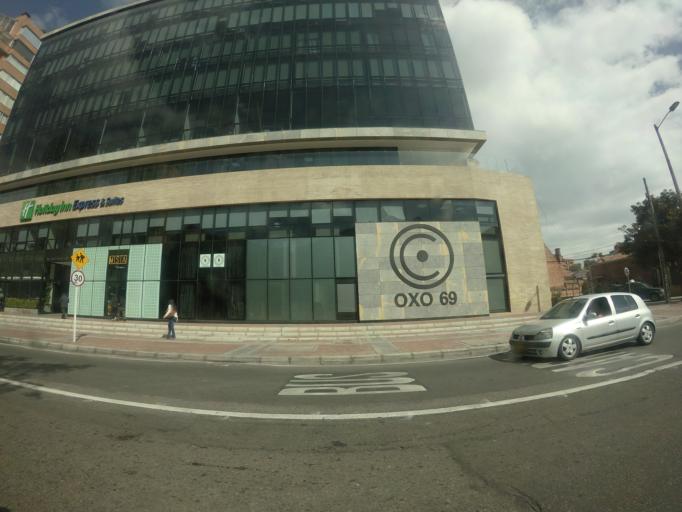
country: CO
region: Bogota D.C.
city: Barrio San Luis
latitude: 4.6512
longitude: -74.0577
